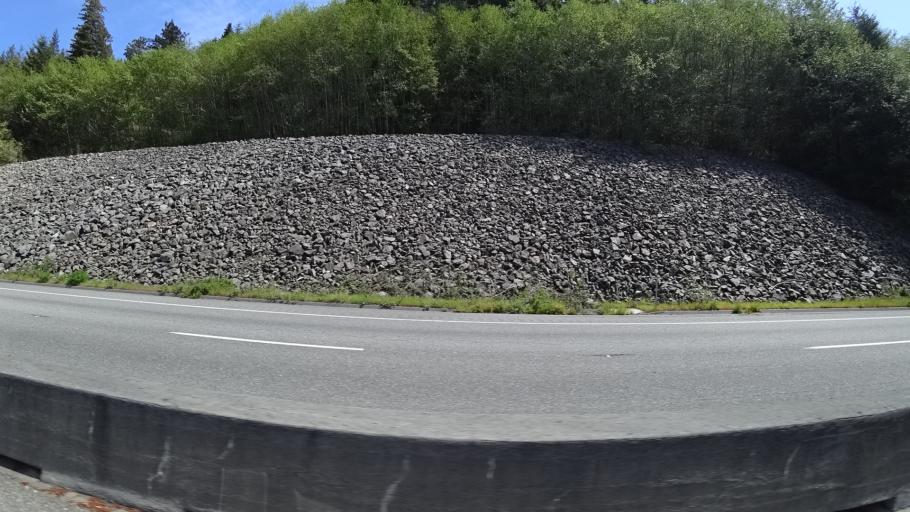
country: US
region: California
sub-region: Humboldt County
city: Westhaven-Moonstone
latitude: 41.3738
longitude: -123.9924
